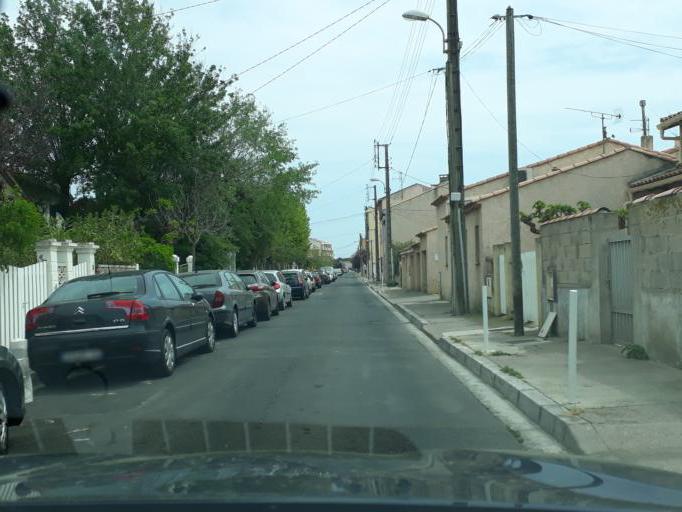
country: FR
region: Languedoc-Roussillon
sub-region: Departement de l'Herault
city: Vias
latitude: 43.2851
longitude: 3.4464
